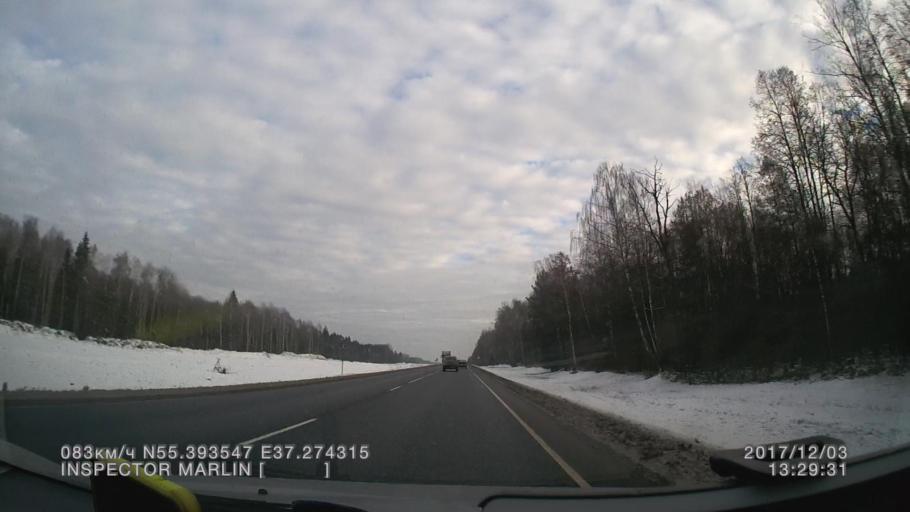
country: RU
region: Moskovskaya
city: Troitsk
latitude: 55.3935
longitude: 37.2748
